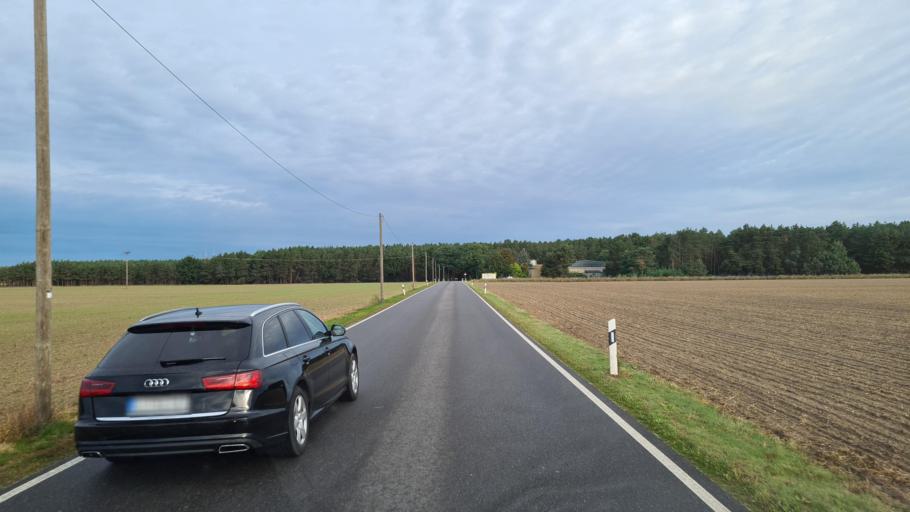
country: DE
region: Brandenburg
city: Luckau
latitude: 51.8846
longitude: 13.7180
